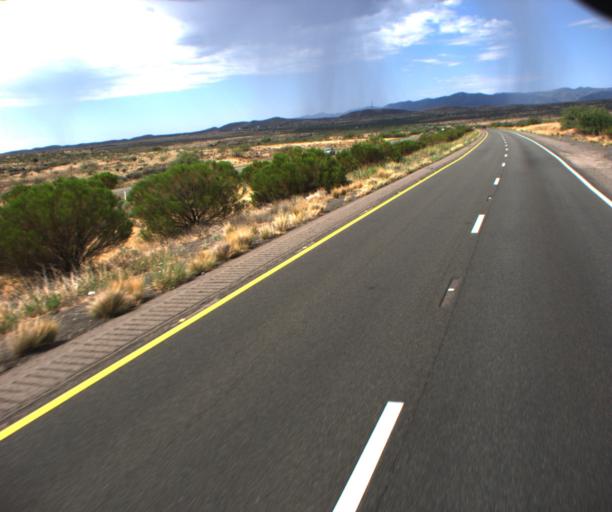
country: US
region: Arizona
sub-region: Yavapai County
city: Spring Valley
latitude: 34.3742
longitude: -112.1078
